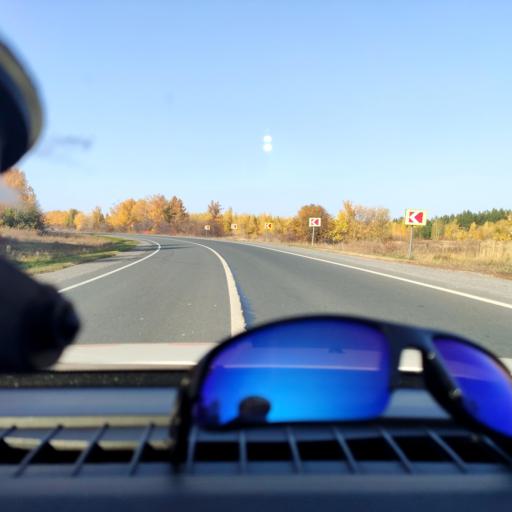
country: RU
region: Samara
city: Volzhskiy
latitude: 53.4654
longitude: 50.1279
